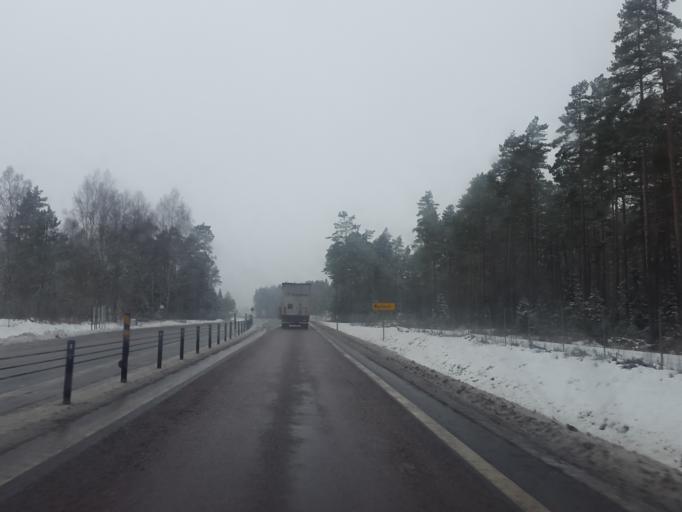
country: SE
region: Joenkoeping
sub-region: Jonkopings Kommun
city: Taberg
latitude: 57.7735
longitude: 14.0509
